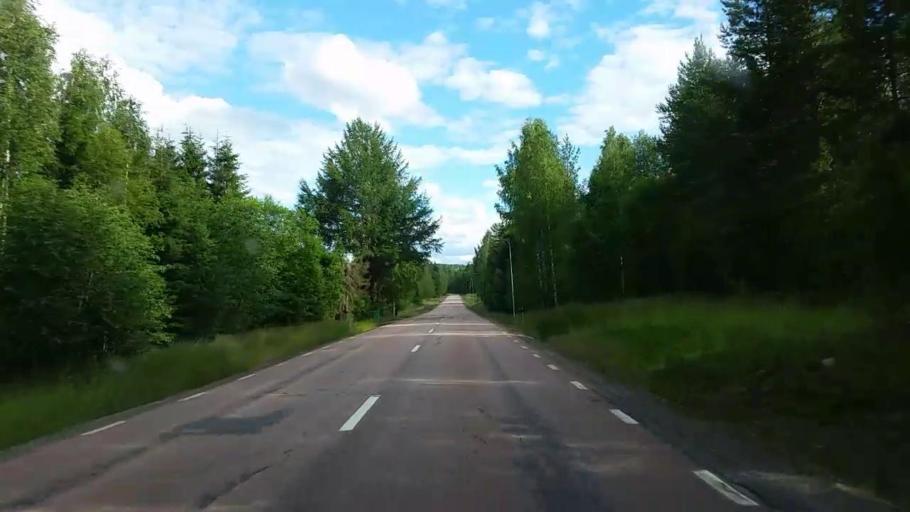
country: SE
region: Gaevleborg
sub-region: Ljusdals Kommun
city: Farila
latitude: 61.9037
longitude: 15.8957
